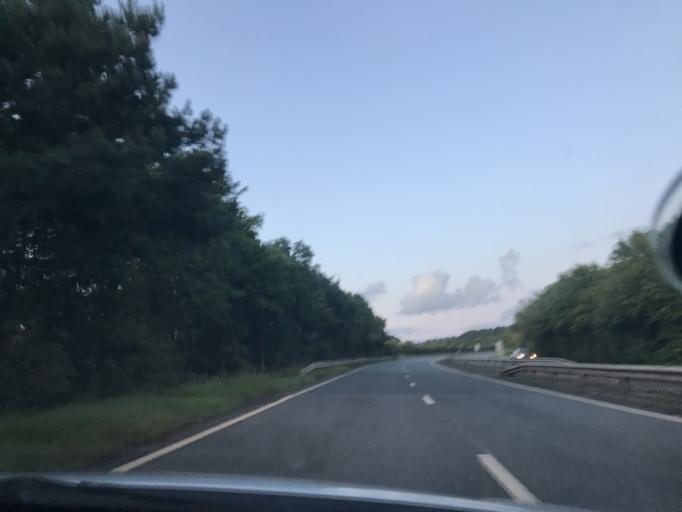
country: GB
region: England
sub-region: Cheshire West and Chester
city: Kelsall
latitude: 53.2116
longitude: -2.7278
